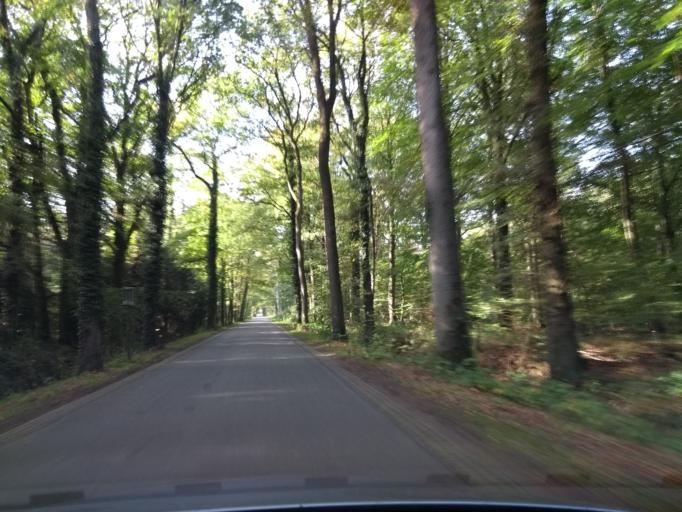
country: NL
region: Gelderland
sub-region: Gemeente Lochem
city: Barchem
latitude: 52.1013
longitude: 6.3938
